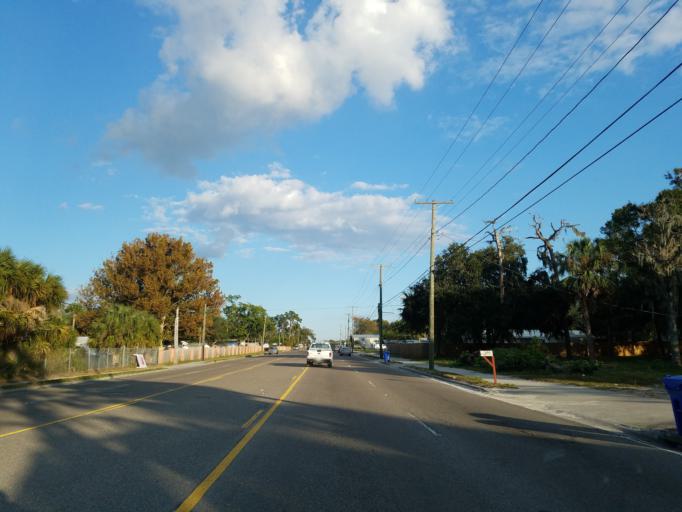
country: US
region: Florida
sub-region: Hillsborough County
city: Gibsonton
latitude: 27.8497
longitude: -82.3605
